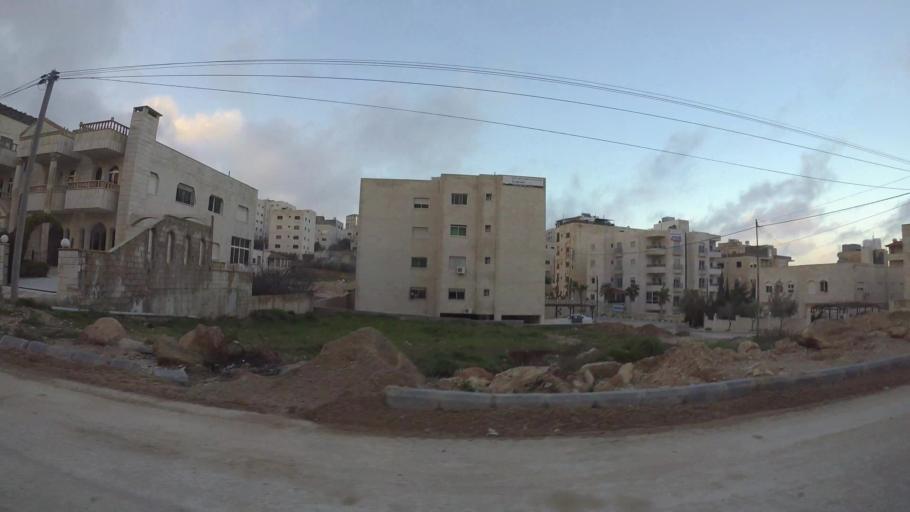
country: JO
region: Amman
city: Al Jubayhah
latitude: 32.0512
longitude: 35.8941
